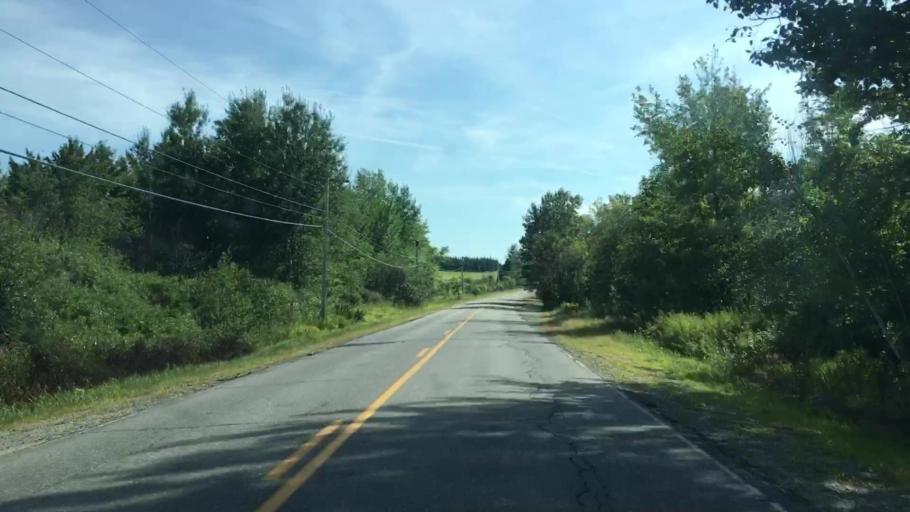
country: US
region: Maine
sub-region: Penobscot County
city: Lincoln
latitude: 45.3228
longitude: -68.5331
